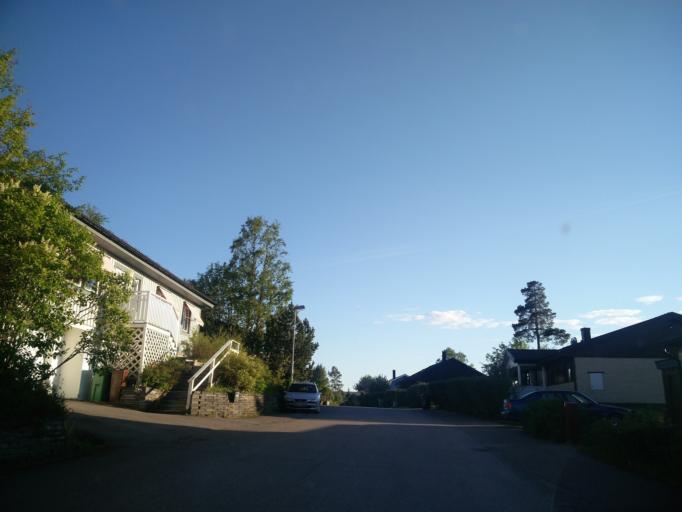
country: SE
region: Vaesternorrland
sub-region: Sundsvalls Kommun
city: Sundsvall
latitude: 62.4058
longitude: 17.2764
